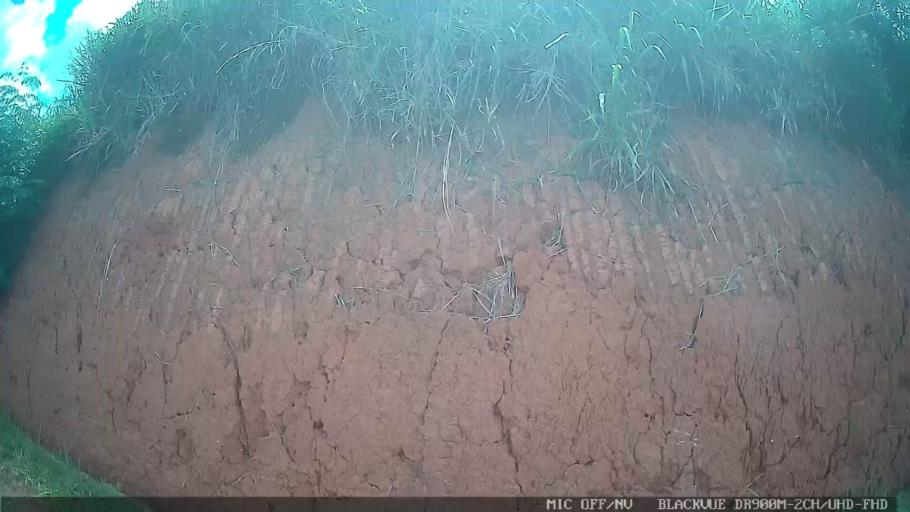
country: BR
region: Sao Paulo
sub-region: Atibaia
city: Atibaia
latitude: -23.0590
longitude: -46.5067
